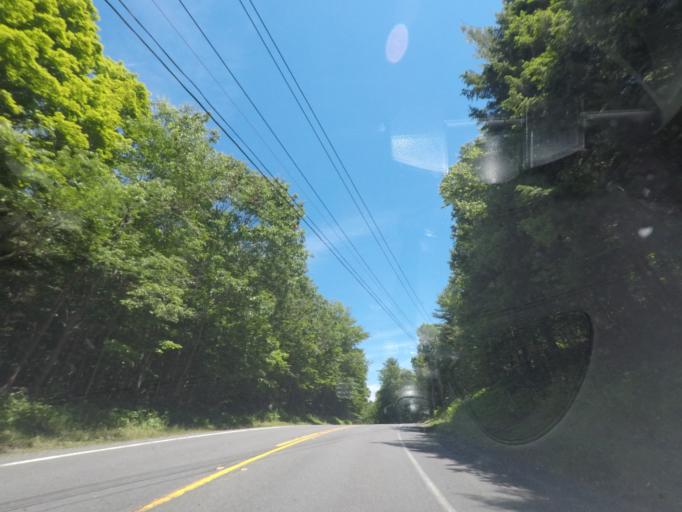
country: US
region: Massachusetts
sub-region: Berkshire County
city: Becket
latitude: 42.2669
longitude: -73.0369
